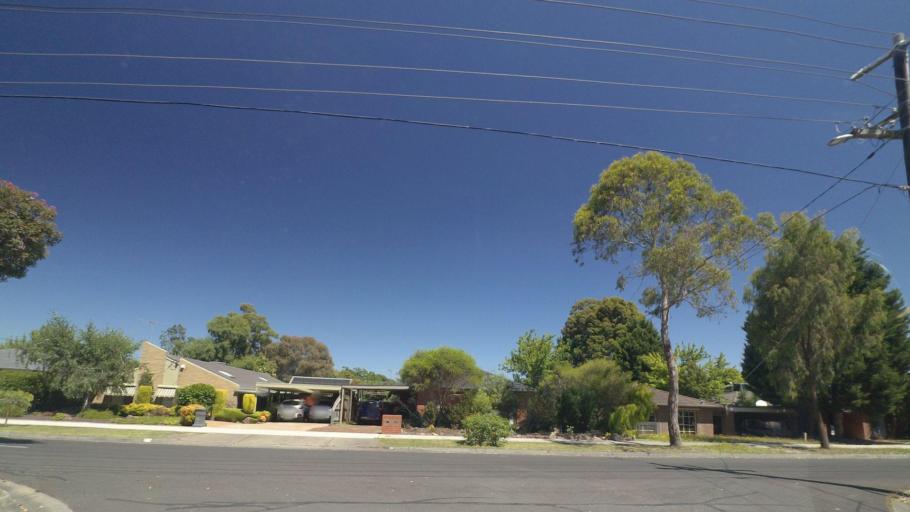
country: AU
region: Victoria
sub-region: Maroondah
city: Warranwood
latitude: -37.7864
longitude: 145.2380
